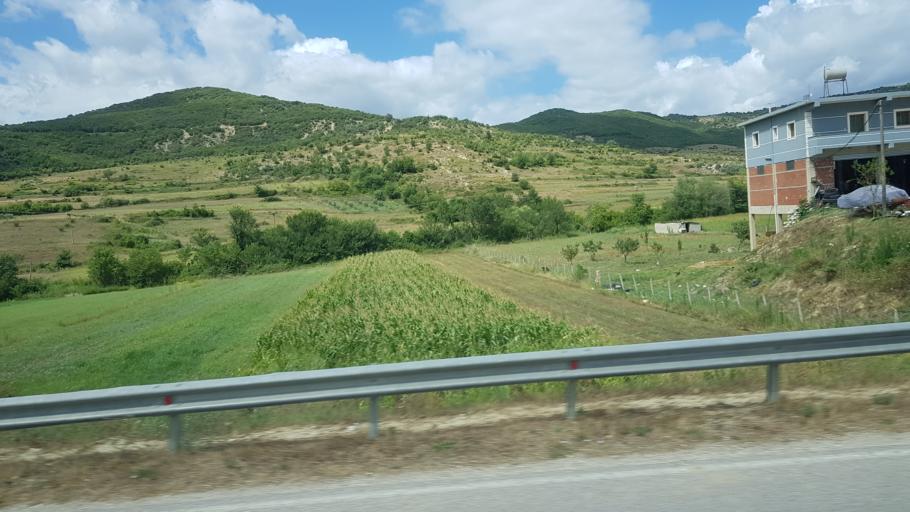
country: AL
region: Gjirokaster
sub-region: Rrethi i Tepelenes
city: Krahes
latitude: 40.4166
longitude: 19.8575
